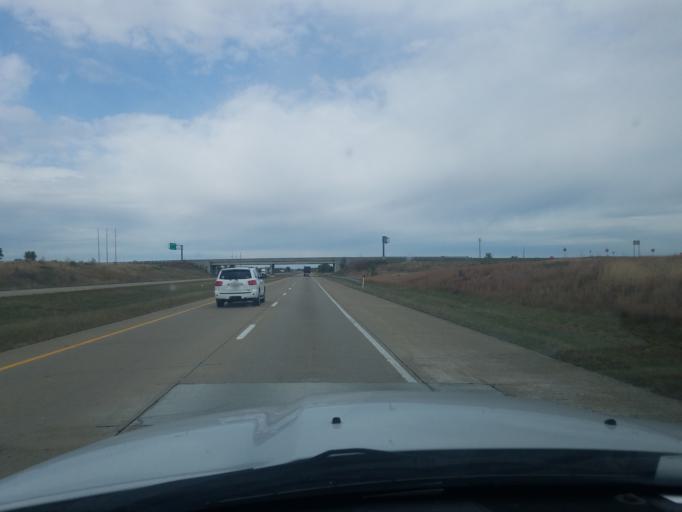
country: US
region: Indiana
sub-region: Vanderburgh County
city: Melody Hill
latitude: 38.0874
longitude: -87.4765
